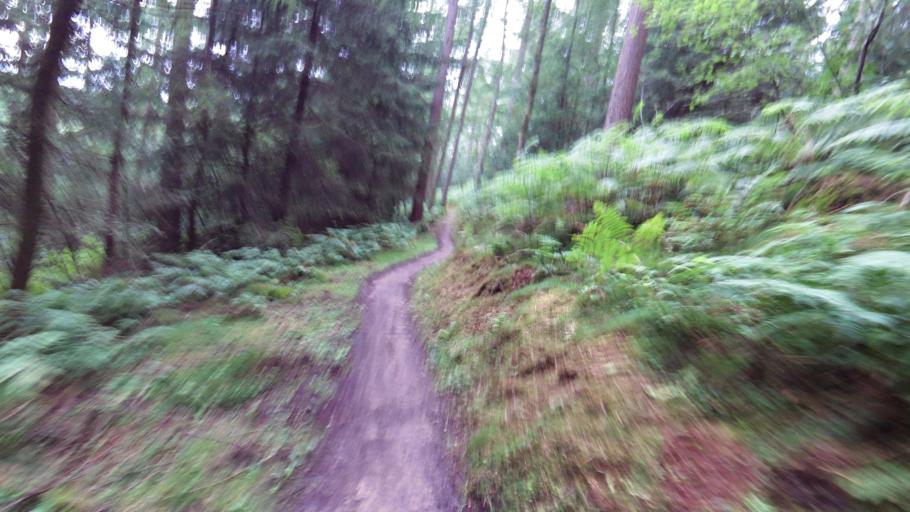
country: GB
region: England
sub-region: North Yorkshire
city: Thornton Dale
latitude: 54.2806
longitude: -0.6843
